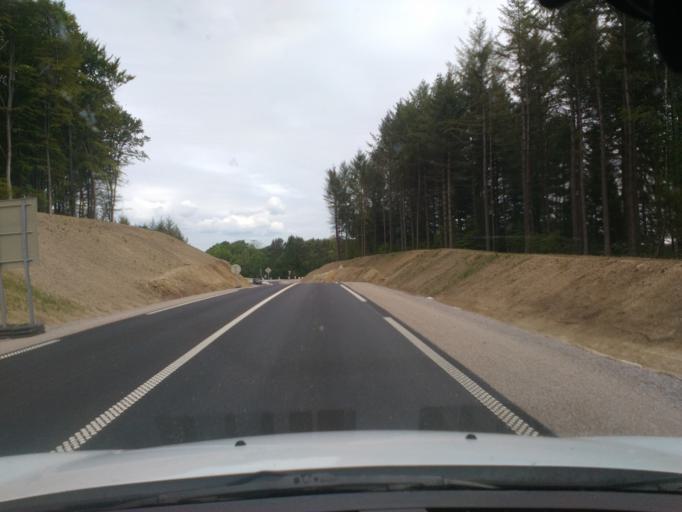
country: FR
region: Lorraine
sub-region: Departement des Vosges
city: Deyvillers
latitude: 48.1807
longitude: 6.4970
